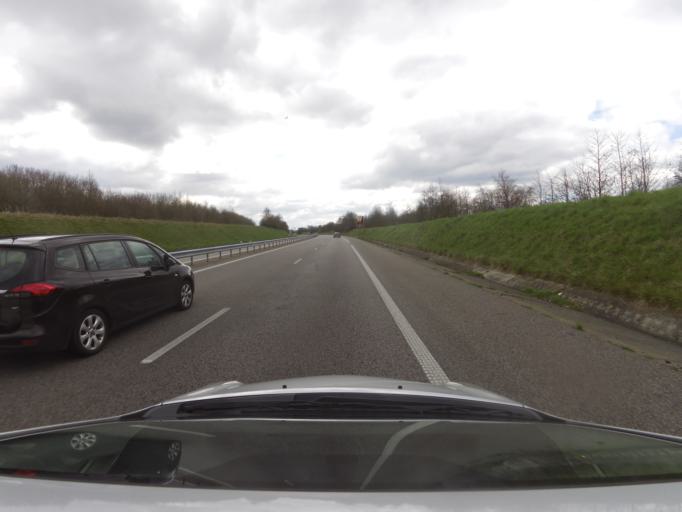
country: FR
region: Haute-Normandie
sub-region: Departement de la Seine-Maritime
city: Saint-Aubin-Routot
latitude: 49.5360
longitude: 0.3182
